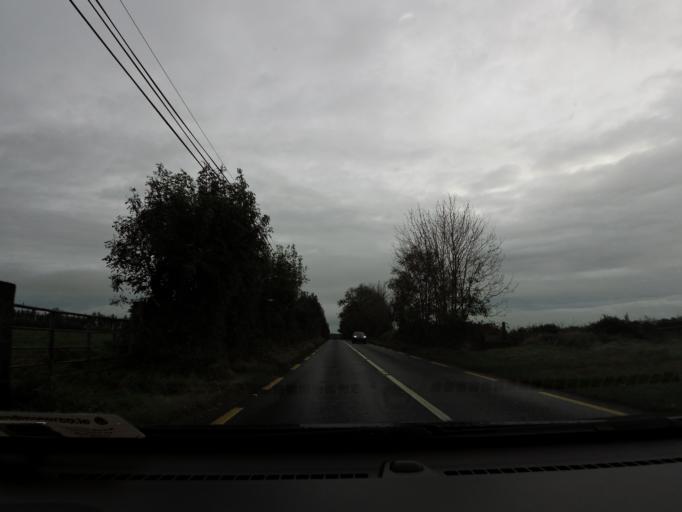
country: IE
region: Connaught
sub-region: County Galway
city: Tuam
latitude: 53.5501
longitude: -8.8086
